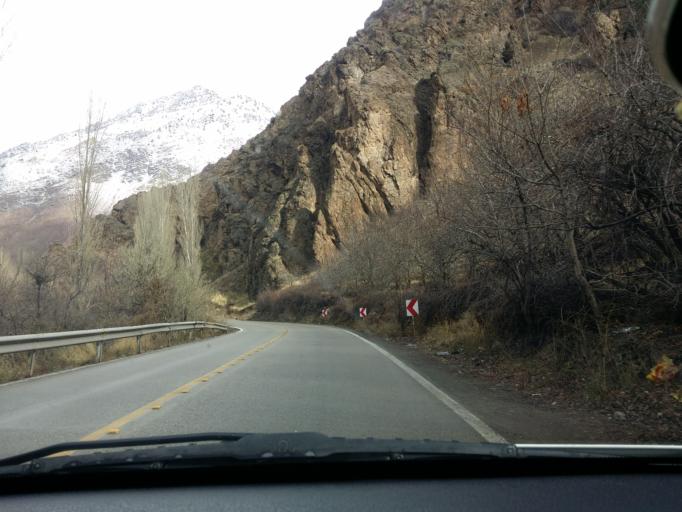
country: IR
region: Tehran
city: Tajrish
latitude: 36.0456
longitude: 51.3127
